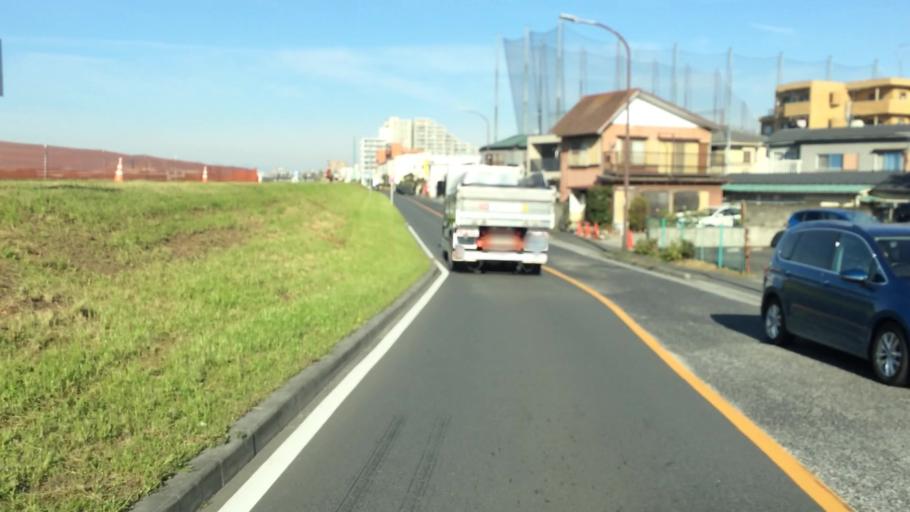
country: JP
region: Tokyo
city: Chofugaoka
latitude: 35.6454
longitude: 139.5263
